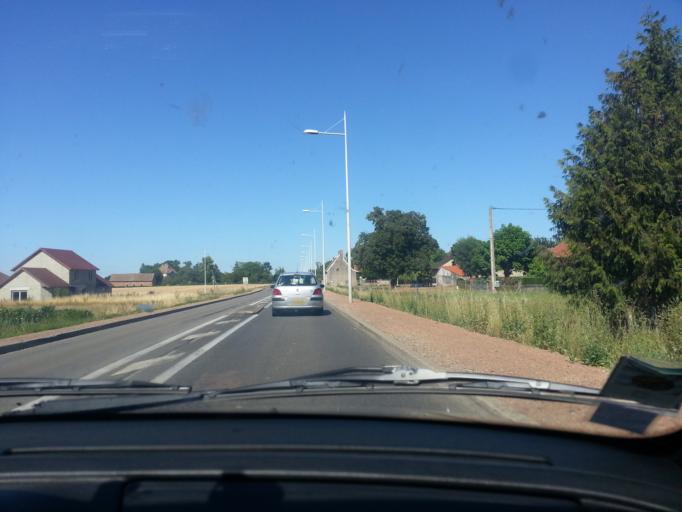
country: FR
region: Bourgogne
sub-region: Departement de Saone-et-Loire
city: Sassenay
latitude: 46.8160
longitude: 4.9614
